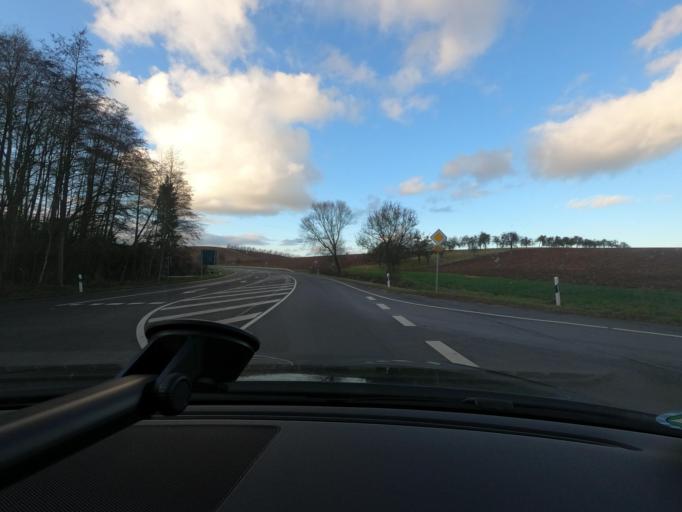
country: DE
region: Thuringia
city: Ferna
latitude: 51.4613
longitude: 10.3002
